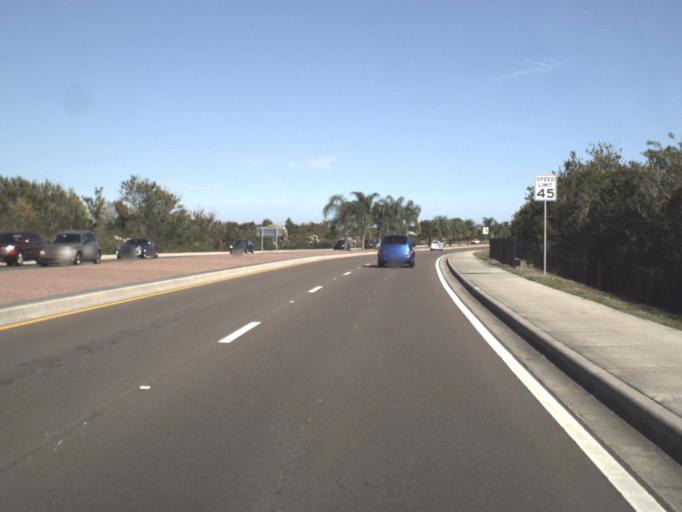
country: US
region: Florida
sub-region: Brevard County
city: South Patrick Shores
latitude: 28.1997
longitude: -80.6847
